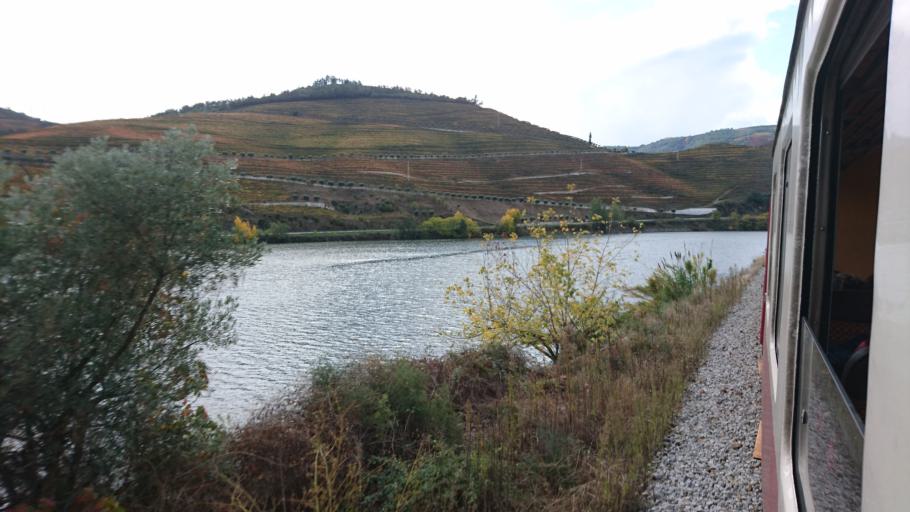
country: PT
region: Viseu
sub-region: Armamar
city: Armamar
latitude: 41.1468
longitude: -7.6910
